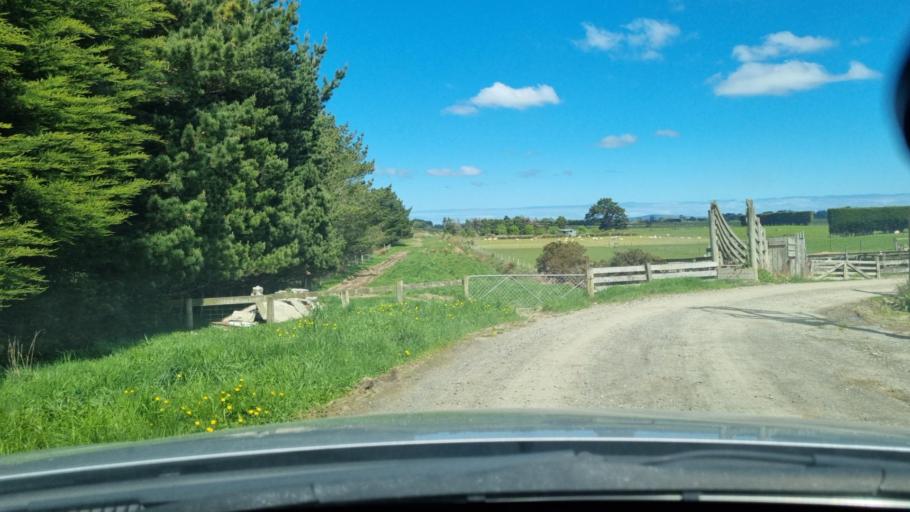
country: NZ
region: Southland
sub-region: Invercargill City
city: Invercargill
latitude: -46.3712
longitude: 168.3237
